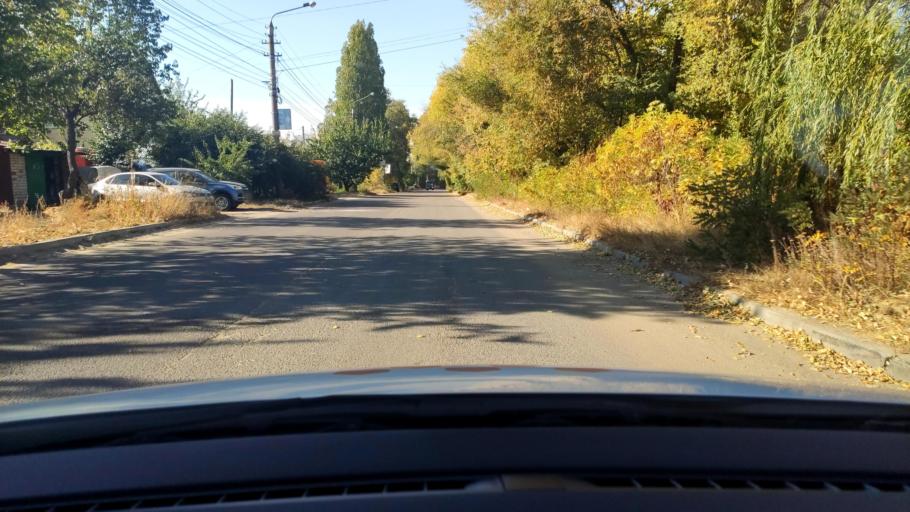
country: RU
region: Voronezj
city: Voronezh
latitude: 51.6822
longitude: 39.1464
